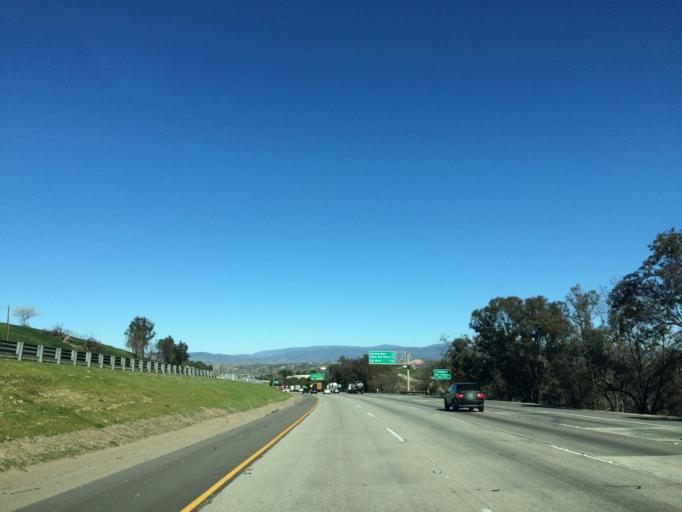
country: US
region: California
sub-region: Los Angeles County
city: Santa Clarita
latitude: 34.3985
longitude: -118.5722
